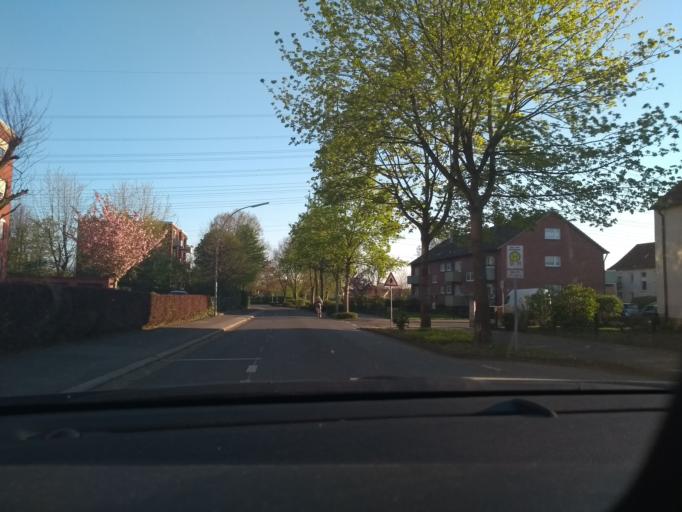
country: DE
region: North Rhine-Westphalia
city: Selm
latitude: 51.6616
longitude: 7.4668
